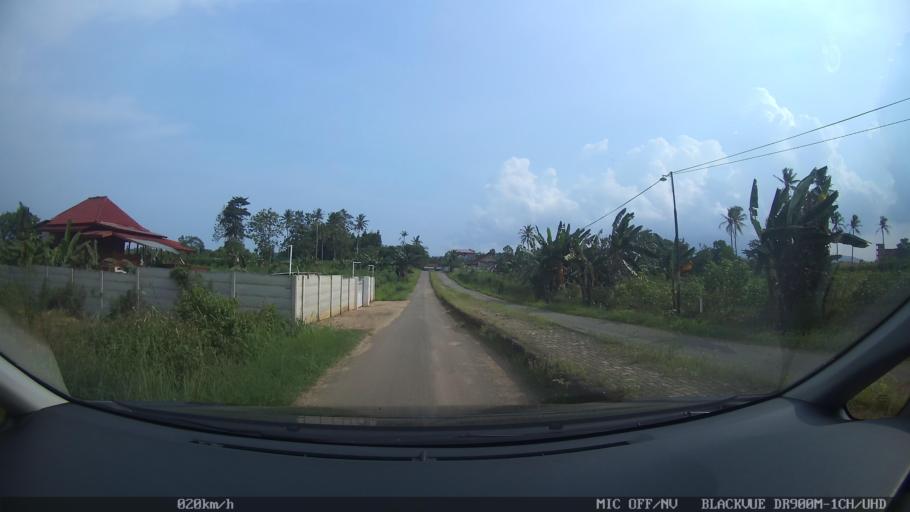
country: ID
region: Lampung
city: Kedaton
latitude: -5.3626
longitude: 105.2139
